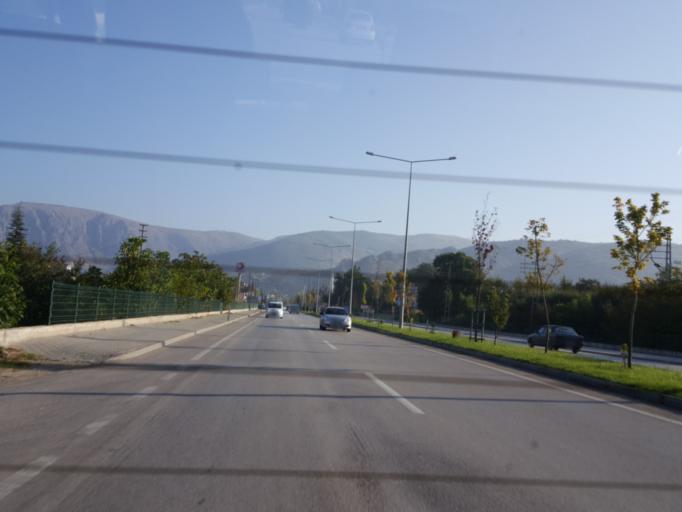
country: TR
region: Amasya
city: Amasya
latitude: 40.5979
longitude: 35.8062
